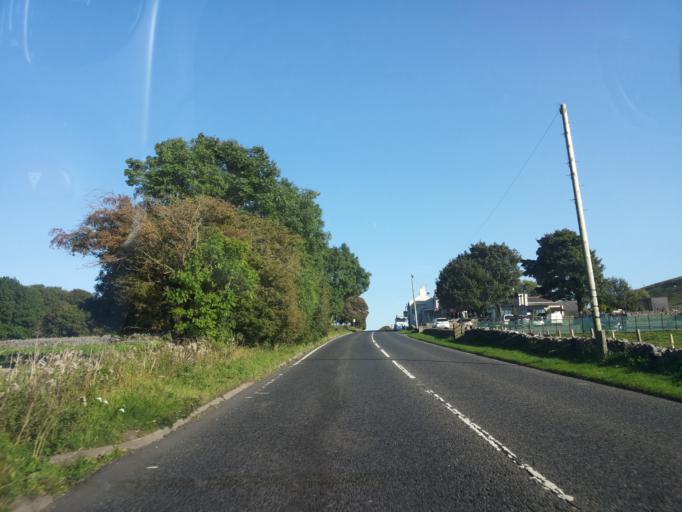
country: GB
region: England
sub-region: Derbyshire
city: Tideswell
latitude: 53.2399
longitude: -1.8063
